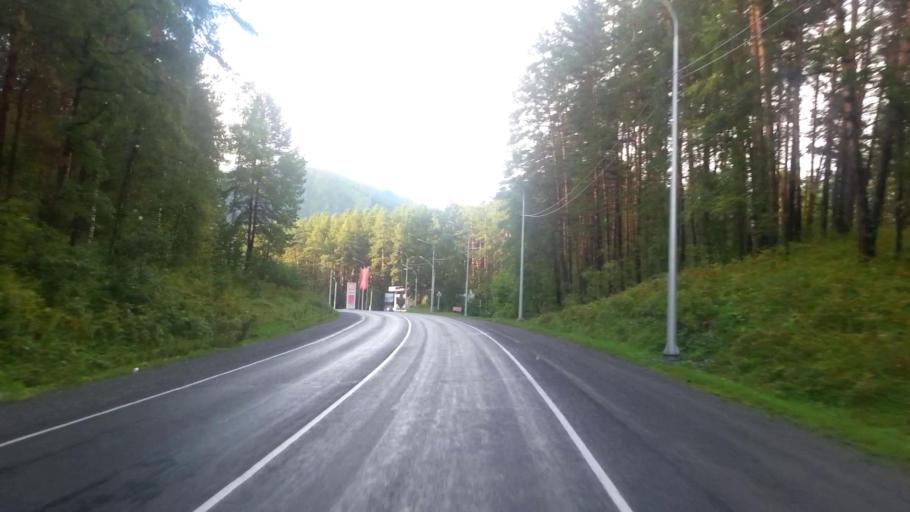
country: RU
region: Altay
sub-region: Mayminskiy Rayon
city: Manzherok
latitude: 51.8241
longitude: 85.7896
